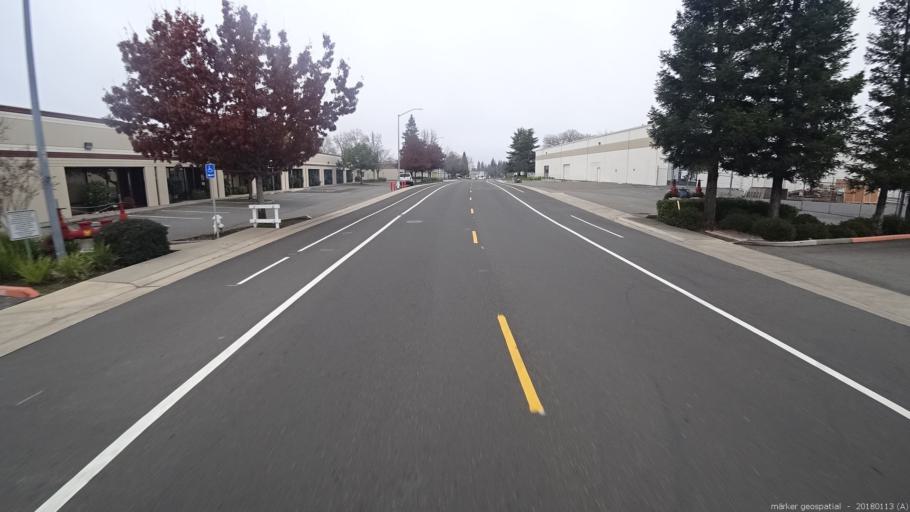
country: US
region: California
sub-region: Sacramento County
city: Gold River
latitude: 38.6017
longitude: -121.2614
